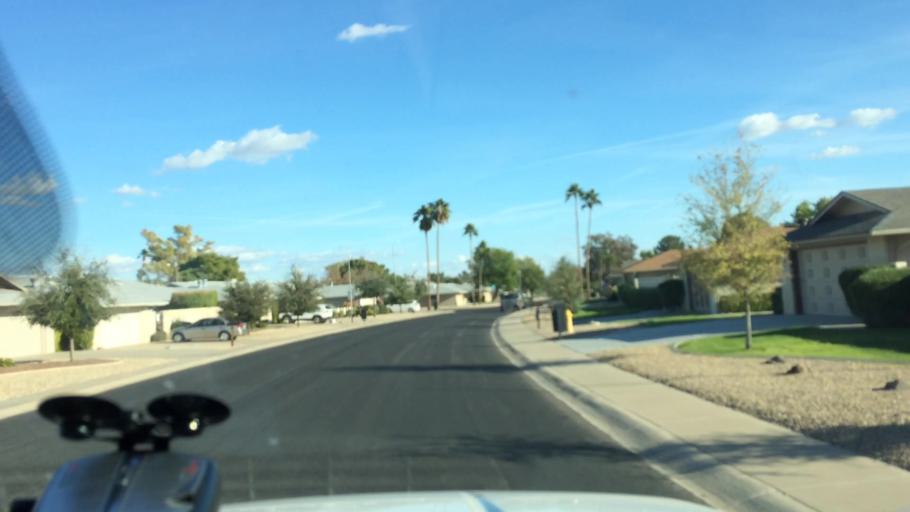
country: US
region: Arizona
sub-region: Maricopa County
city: Sun City West
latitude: 33.6550
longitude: -112.3339
